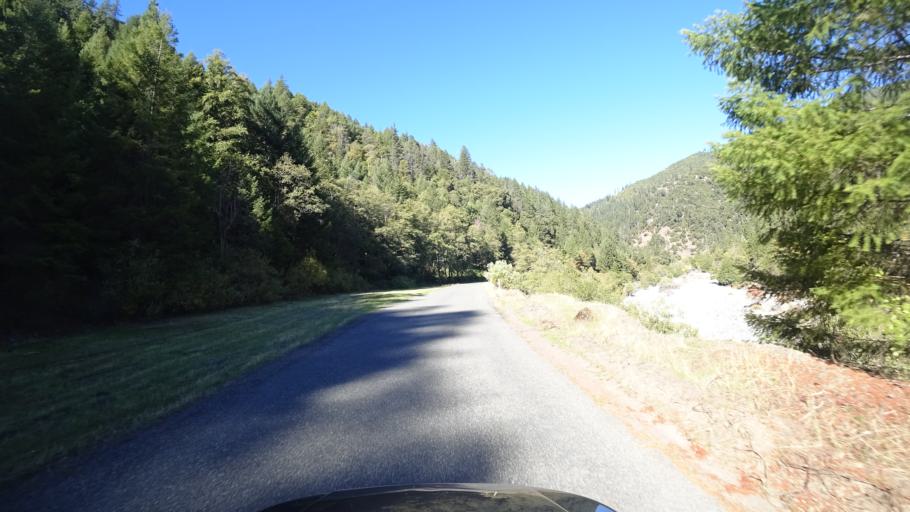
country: US
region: California
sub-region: Humboldt County
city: Willow Creek
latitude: 41.2390
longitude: -123.2815
